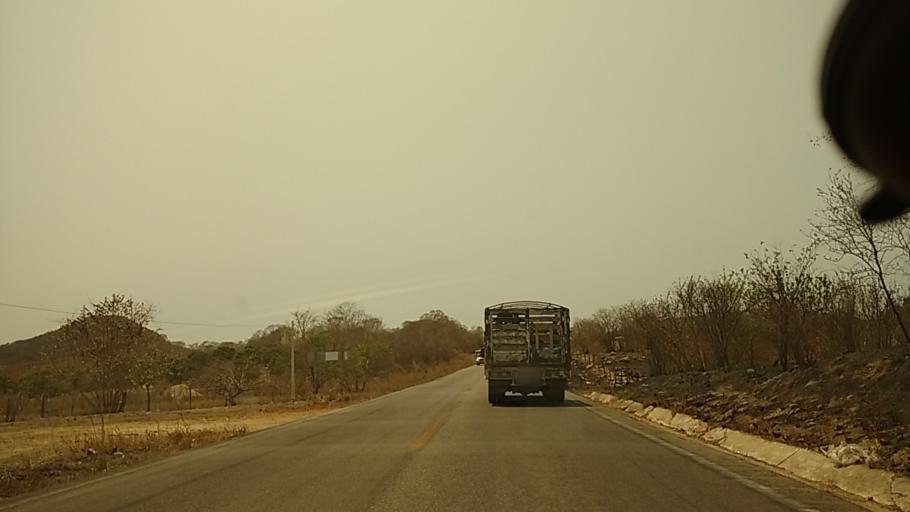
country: MX
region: Guerrero
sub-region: Tecpan de Galeana
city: Villa Rotaria
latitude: 17.2685
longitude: -100.9893
